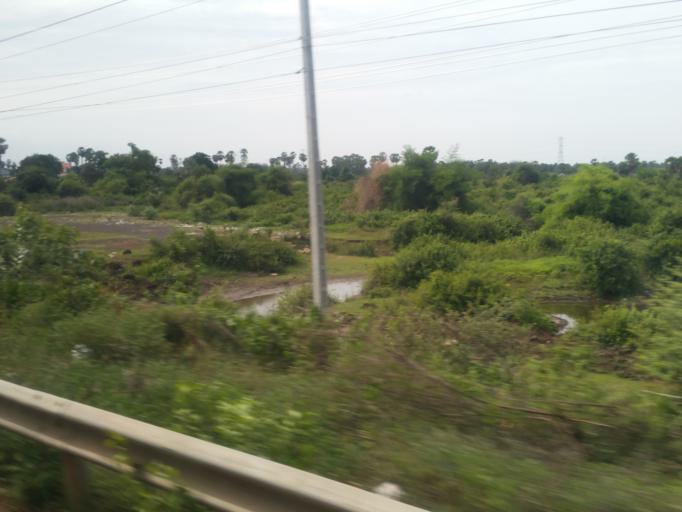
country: KH
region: Kampong Cham
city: Kampong Cham
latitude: 12.0549
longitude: 105.2803
